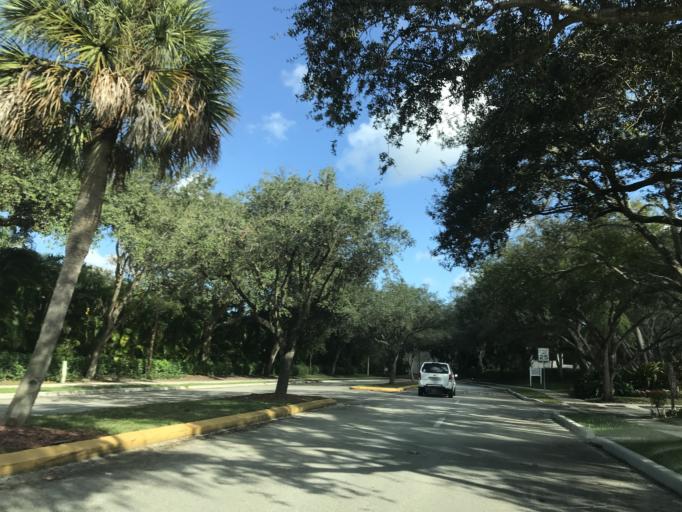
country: US
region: Florida
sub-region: Broward County
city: Coconut Creek
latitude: 26.2549
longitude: -80.1861
